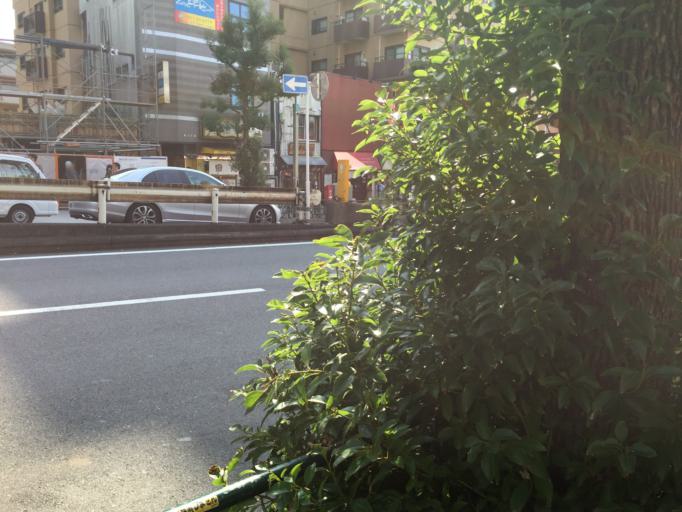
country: JP
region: Tokyo
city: Tokyo
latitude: 35.6346
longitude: 139.7124
